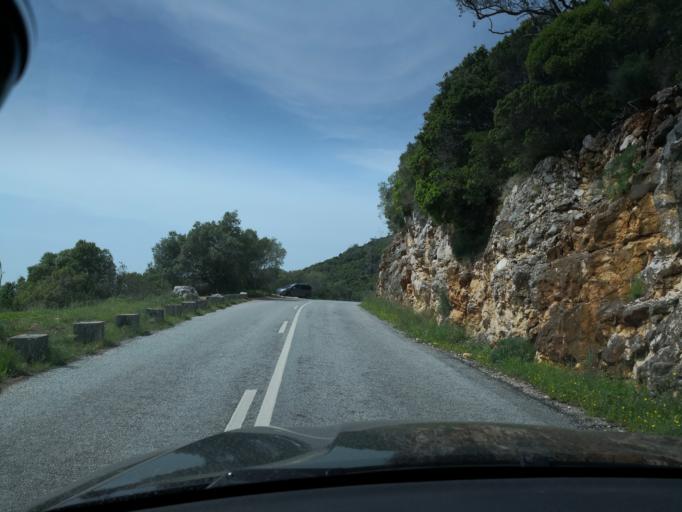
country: PT
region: Setubal
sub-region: Palmela
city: Quinta do Anjo
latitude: 38.4787
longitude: -8.9851
